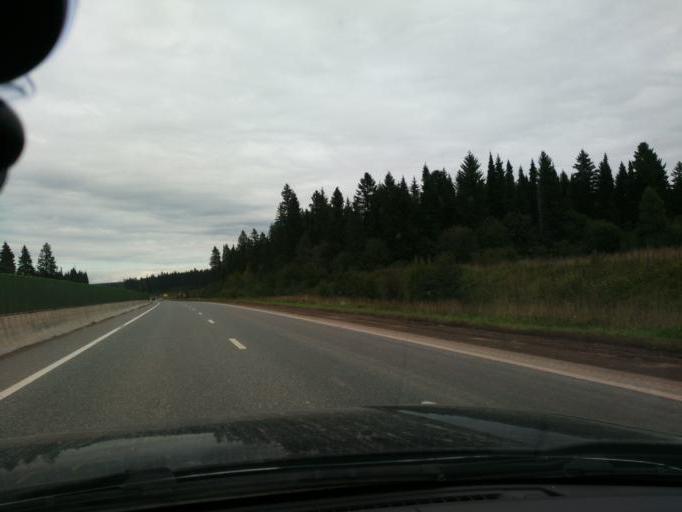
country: RU
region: Perm
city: Ferma
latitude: 57.9423
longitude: 56.3771
